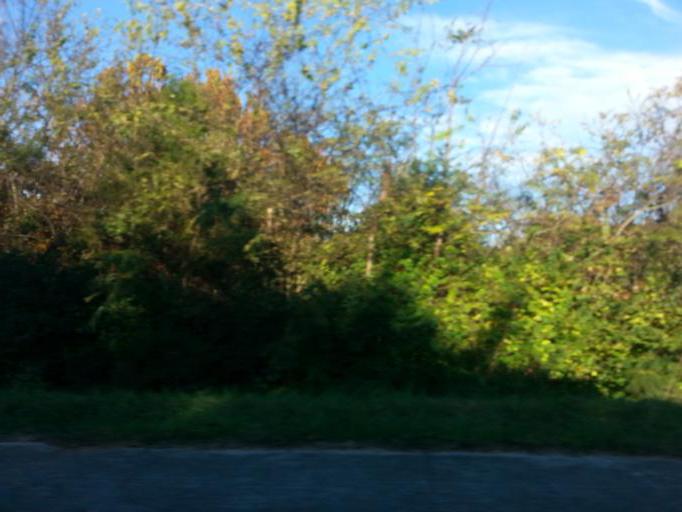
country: US
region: Tennessee
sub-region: Blount County
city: Louisville
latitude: 35.8688
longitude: -84.0638
